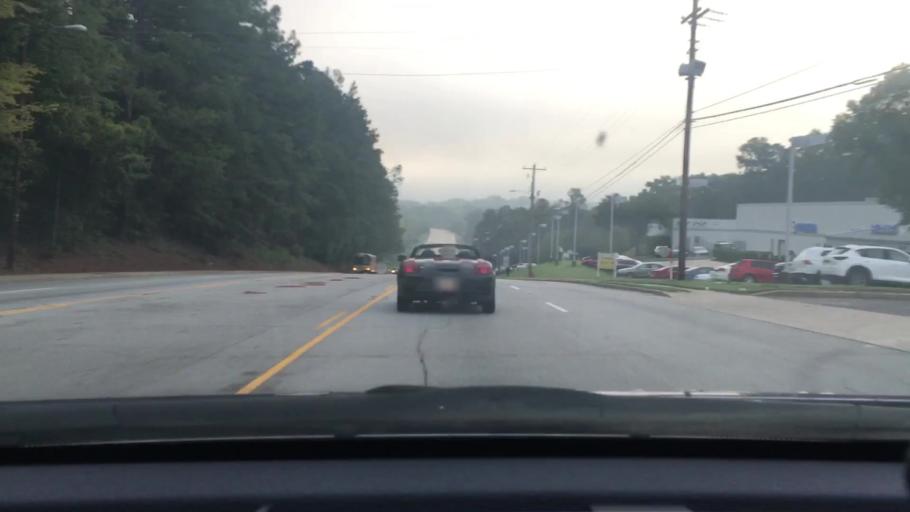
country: US
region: South Carolina
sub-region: Lexington County
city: West Columbia
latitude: 34.0250
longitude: -81.0752
